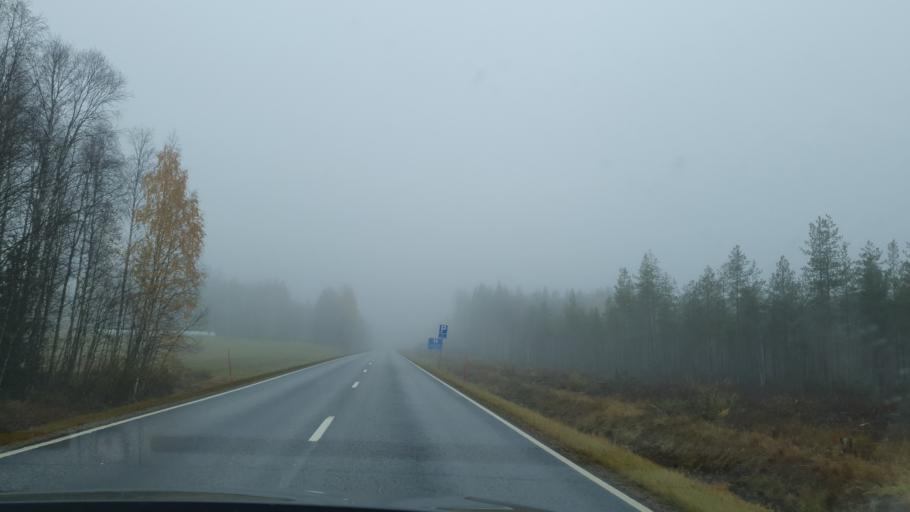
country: FI
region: Lapland
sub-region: Rovaniemi
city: Rovaniemi
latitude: 66.7963
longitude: 25.4149
